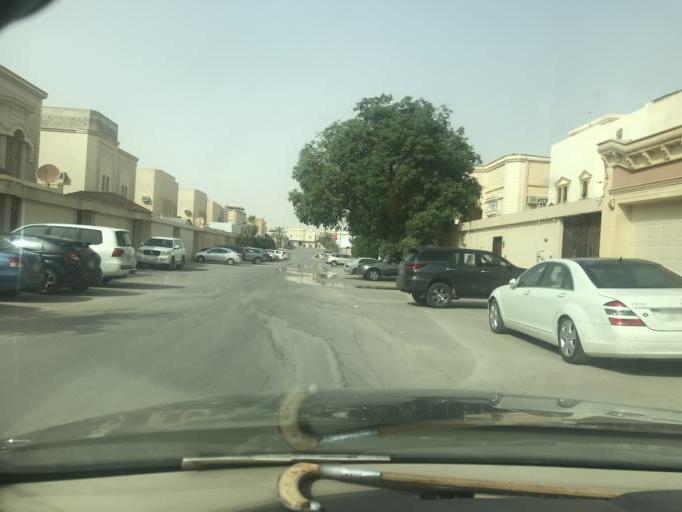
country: SA
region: Ar Riyad
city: Riyadh
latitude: 24.7557
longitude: 46.7698
